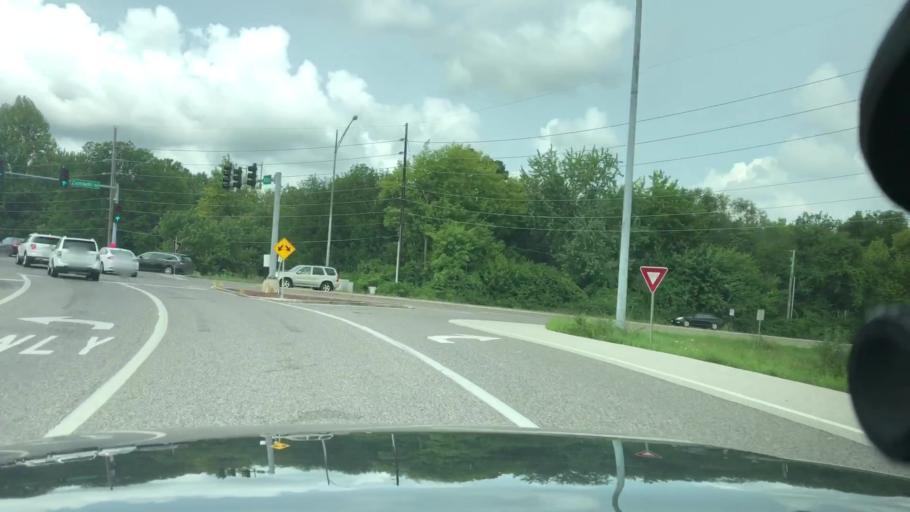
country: US
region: Missouri
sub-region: Saint Charles County
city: Saint Charles
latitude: 38.7883
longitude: -90.5326
